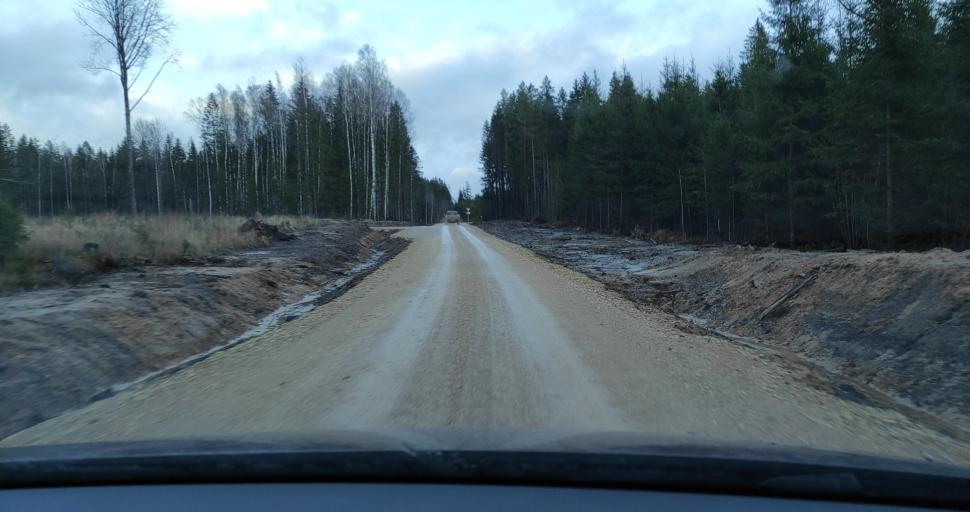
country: LV
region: Skrunda
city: Skrunda
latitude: 56.7421
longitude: 22.2011
